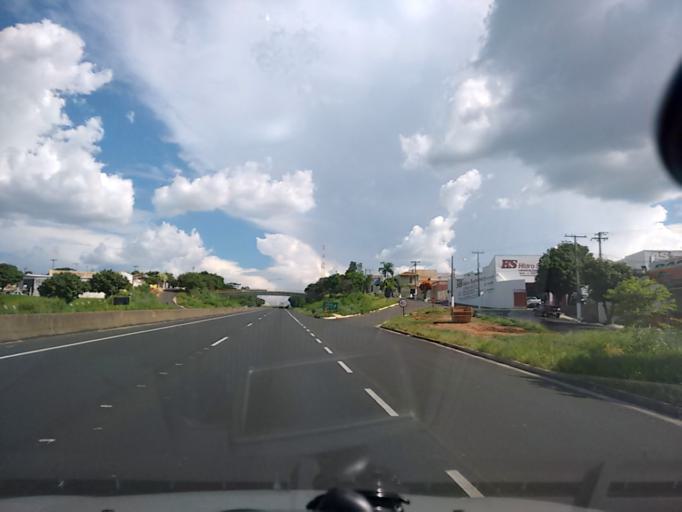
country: BR
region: Sao Paulo
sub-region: Marilia
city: Marilia
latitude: -22.2013
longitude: -49.9646
